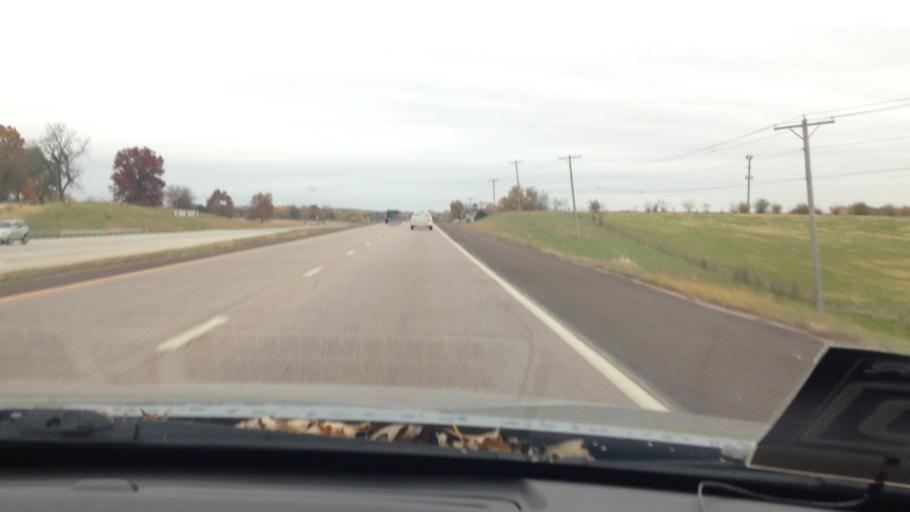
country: US
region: Kansas
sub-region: Leavenworth County
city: Basehor
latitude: 39.1563
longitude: -94.9009
